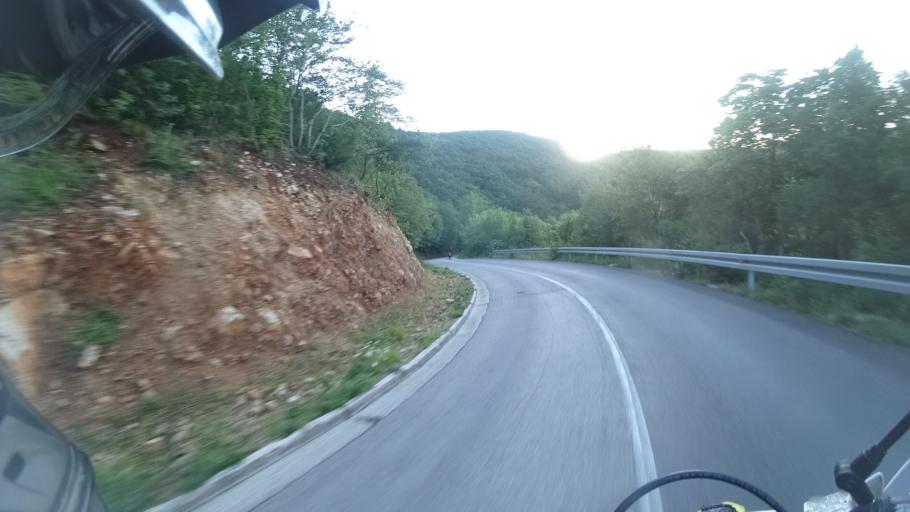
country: HR
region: Sibensko-Kniniska
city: Knin
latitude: 43.9053
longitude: 16.3983
